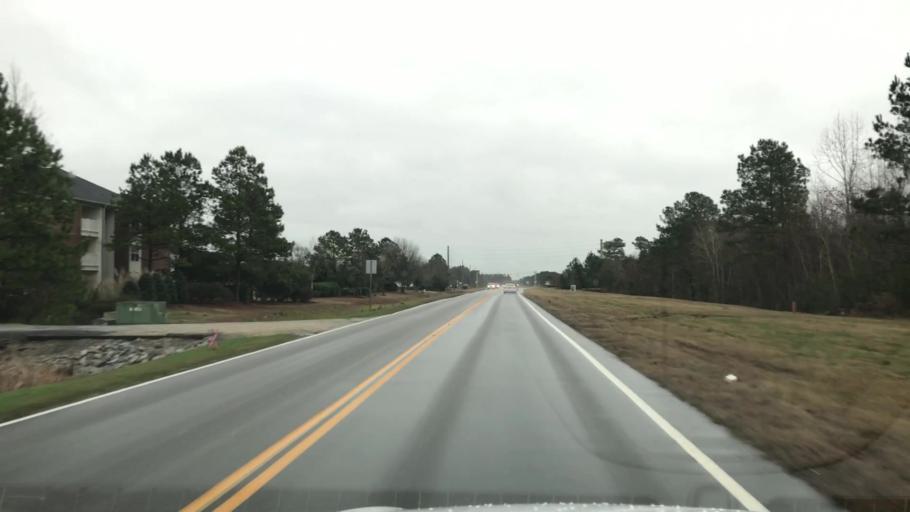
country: US
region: South Carolina
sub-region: Horry County
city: Myrtle Beach
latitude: 33.7348
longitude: -78.9009
